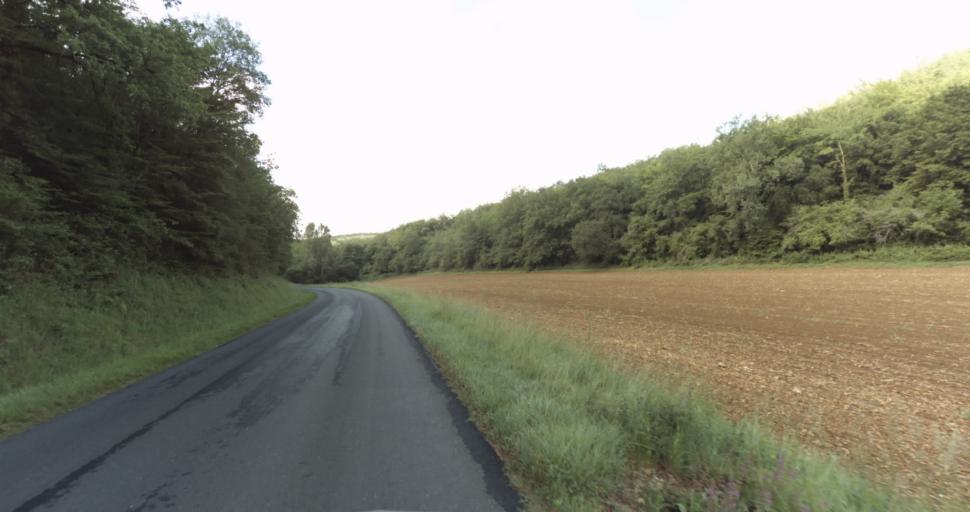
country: FR
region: Aquitaine
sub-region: Departement de la Dordogne
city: Lalinde
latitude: 44.8689
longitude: 0.7733
